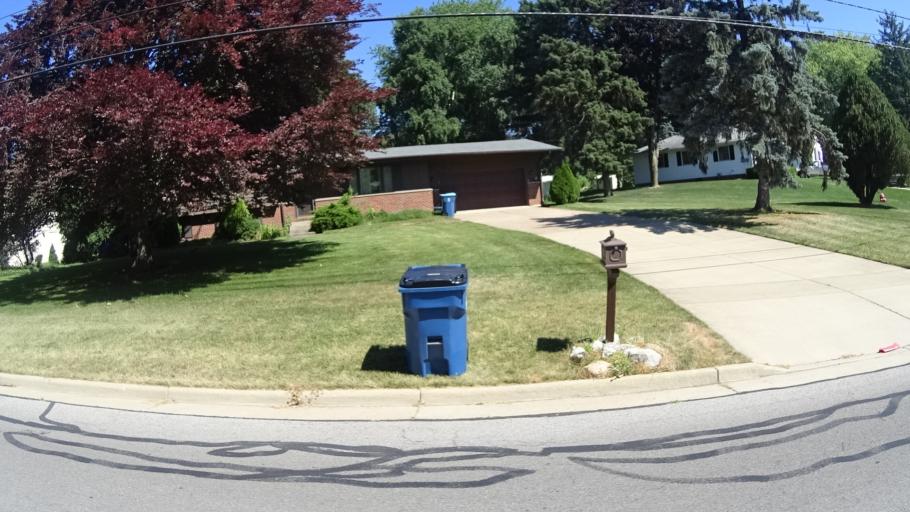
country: US
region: Ohio
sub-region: Erie County
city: Huron
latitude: 41.3768
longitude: -82.5611
